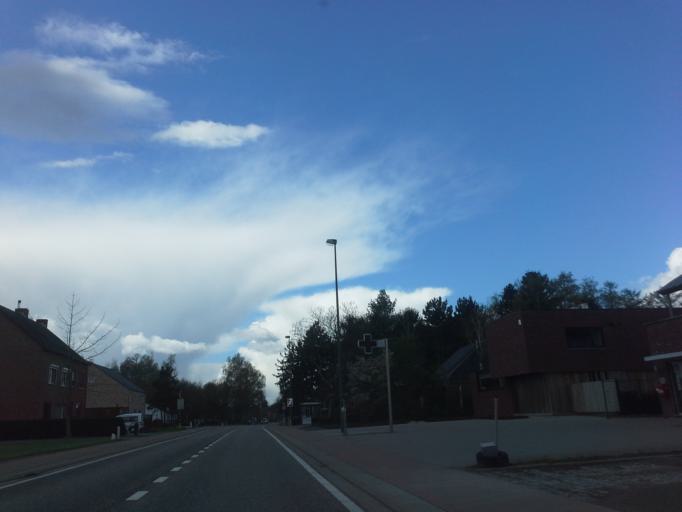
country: BE
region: Flanders
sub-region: Provincie Limburg
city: Tessenderlo
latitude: 51.0836
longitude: 5.1027
